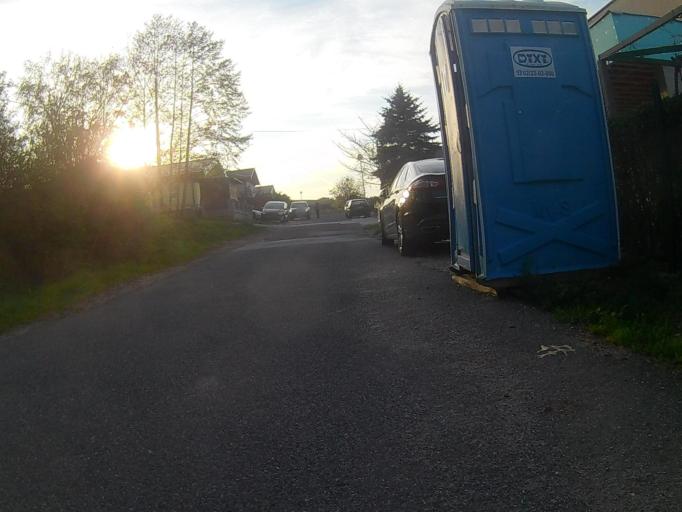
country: SI
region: Maribor
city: Pekre
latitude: 46.5376
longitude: 15.5891
